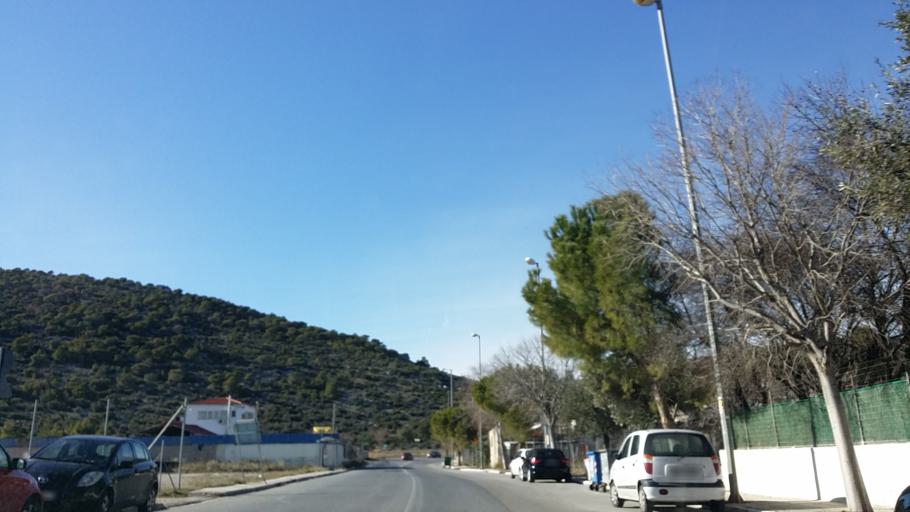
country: GR
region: Attica
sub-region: Nomarchia Dytikis Attikis
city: Fyli
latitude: 38.0970
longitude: 23.6842
